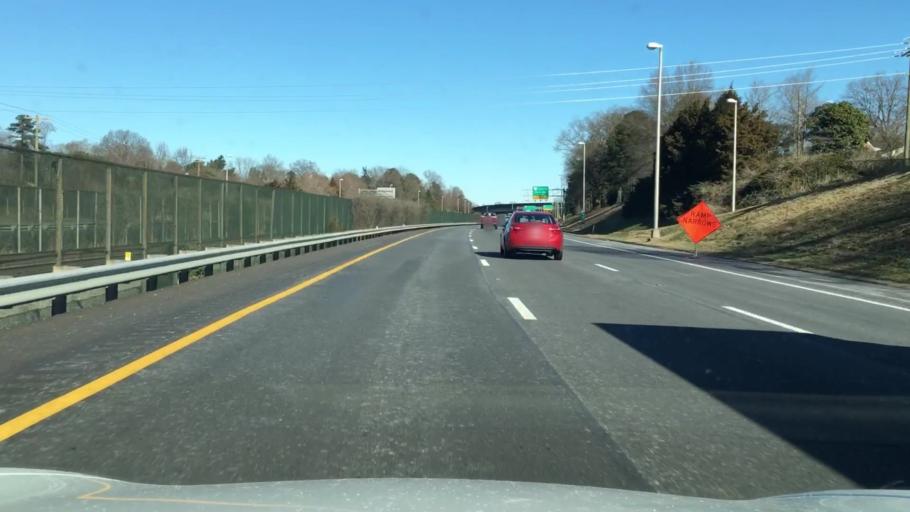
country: US
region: Virginia
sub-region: City of Richmond
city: Richmond
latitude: 37.5479
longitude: -77.4913
